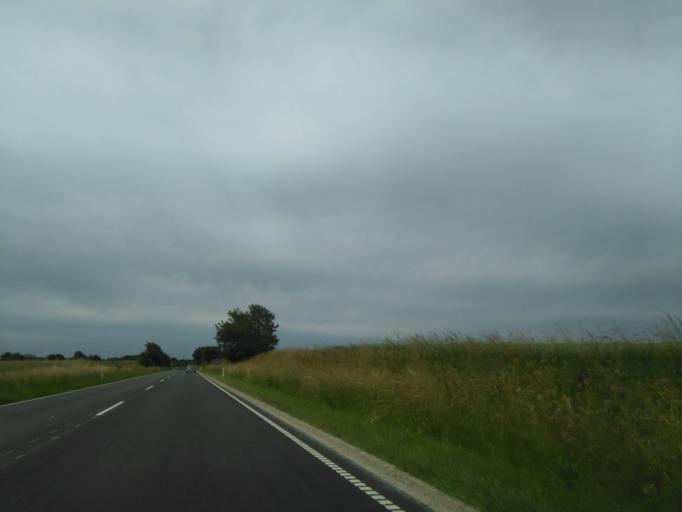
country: DK
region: Central Jutland
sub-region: Arhus Kommune
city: Tranbjerg
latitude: 56.0725
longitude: 10.1029
